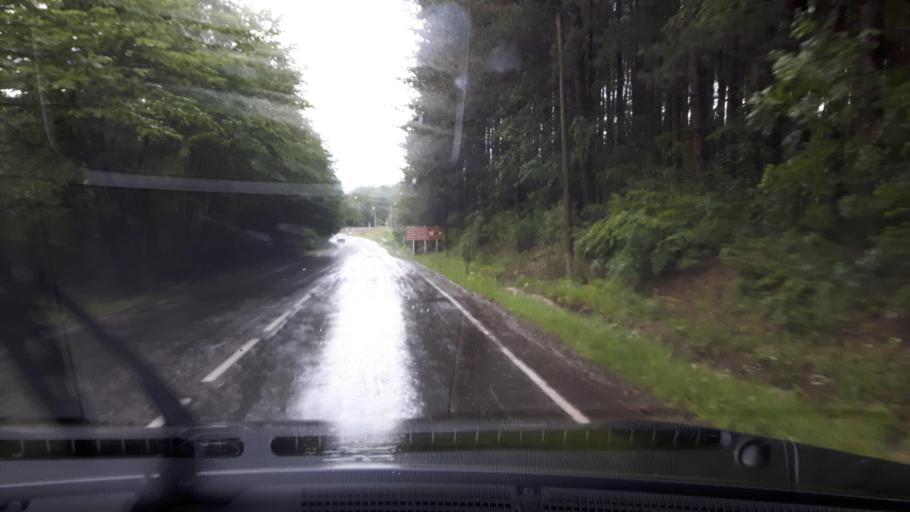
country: GE
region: Kakheti
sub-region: Telavi
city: Telavi
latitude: 41.9133
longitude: 45.3866
